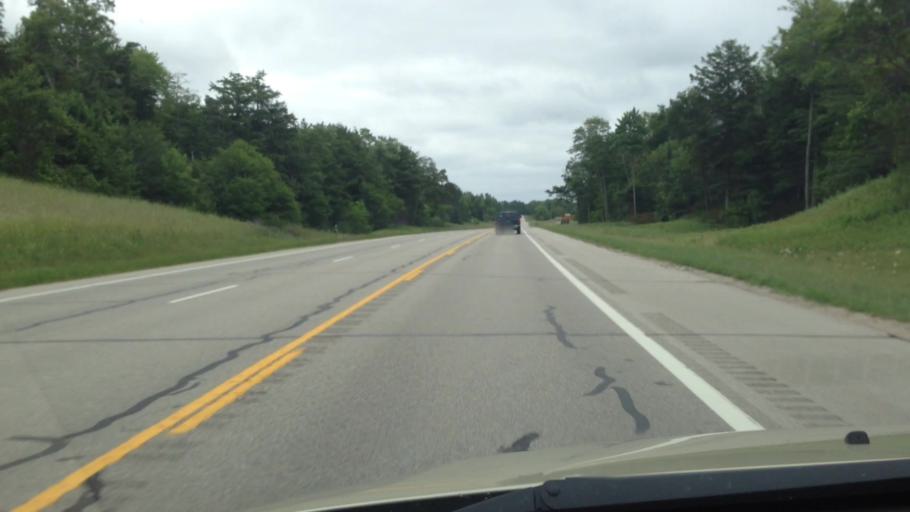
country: US
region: Michigan
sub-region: Mackinac County
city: Saint Ignace
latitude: 46.0144
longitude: -85.0166
